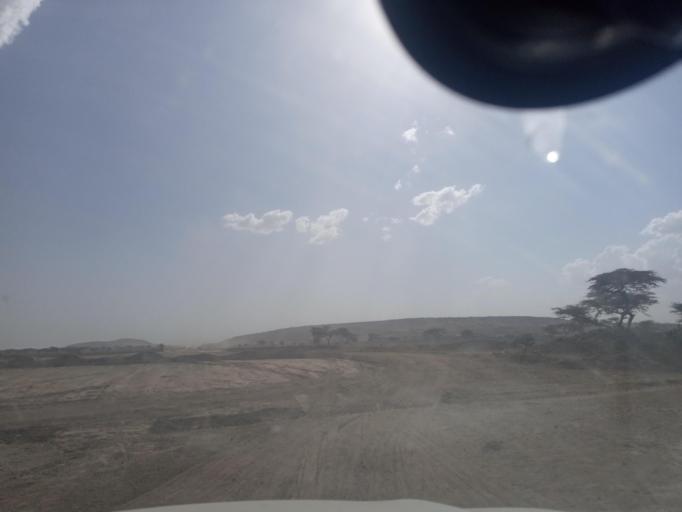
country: ET
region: Oromiya
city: Ziway
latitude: 7.8272
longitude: 38.6489
